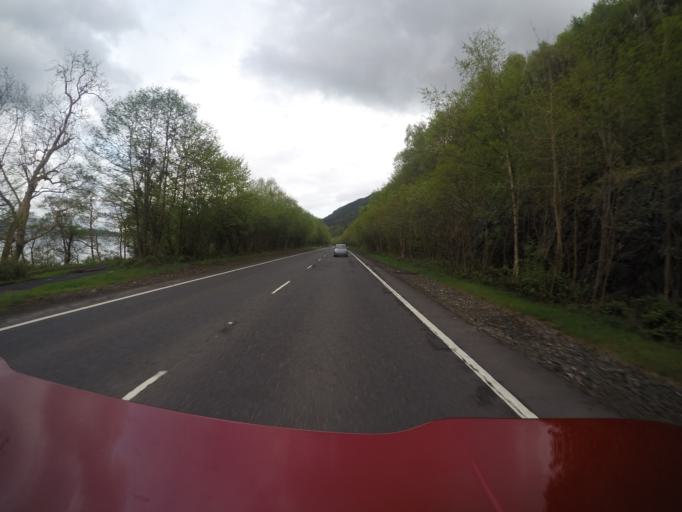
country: GB
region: Scotland
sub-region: Argyll and Bute
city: Helensburgh
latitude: 56.1247
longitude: -4.6530
